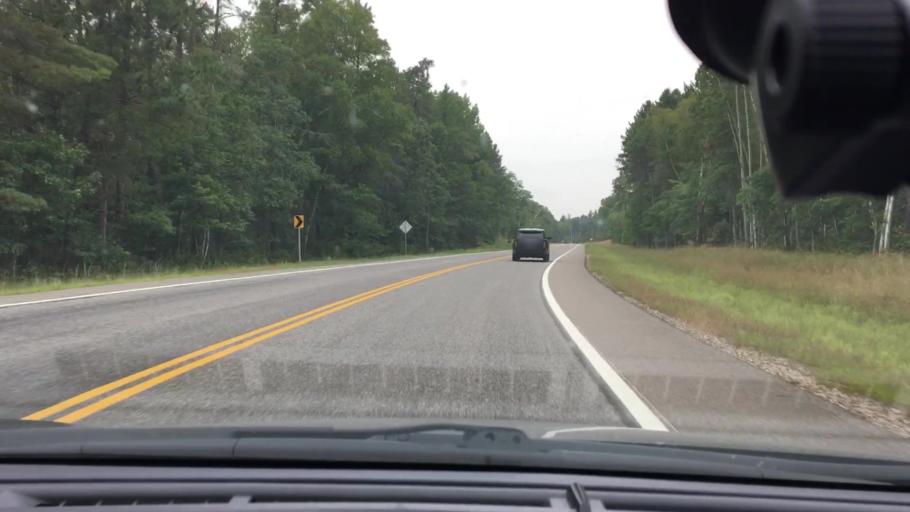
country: US
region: Minnesota
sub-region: Crow Wing County
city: Cross Lake
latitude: 46.6613
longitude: -94.0350
